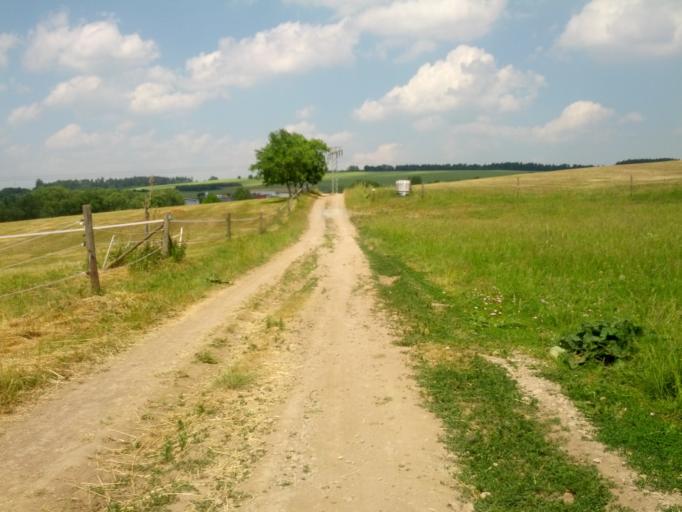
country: DE
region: Thuringia
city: Eisenach
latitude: 50.9968
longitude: 10.3217
